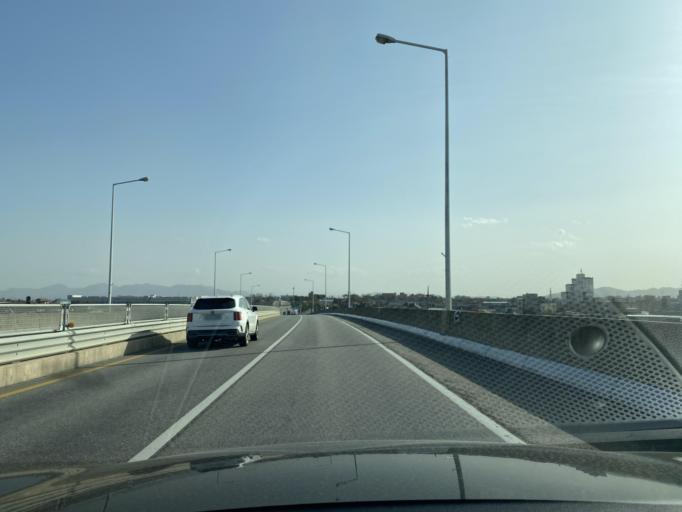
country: KR
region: Chungcheongnam-do
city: Yesan
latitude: 36.6911
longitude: 126.7381
